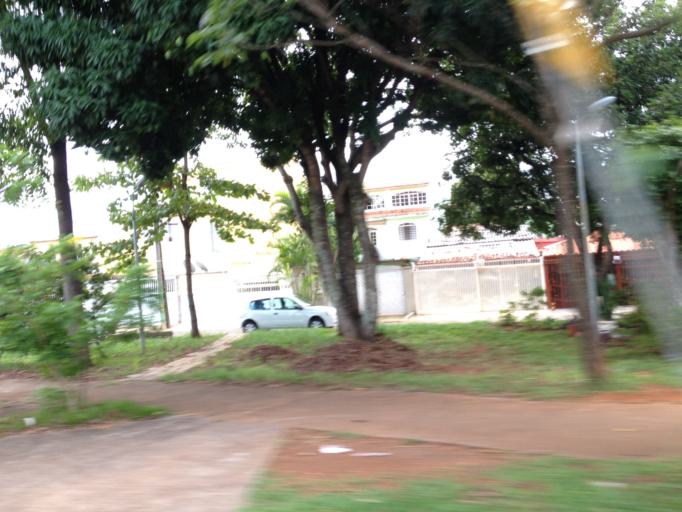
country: BR
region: Federal District
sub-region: Brasilia
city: Brasilia
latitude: -15.7861
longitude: -47.9346
